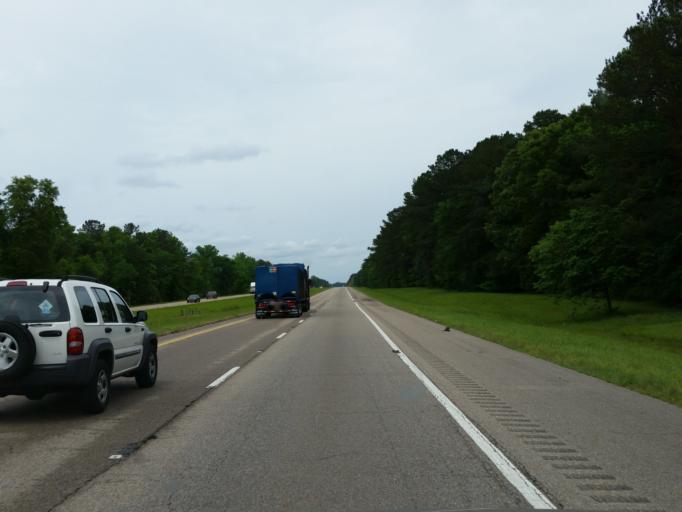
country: US
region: Mississippi
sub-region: Clarke County
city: Stonewall
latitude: 31.9929
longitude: -88.9439
